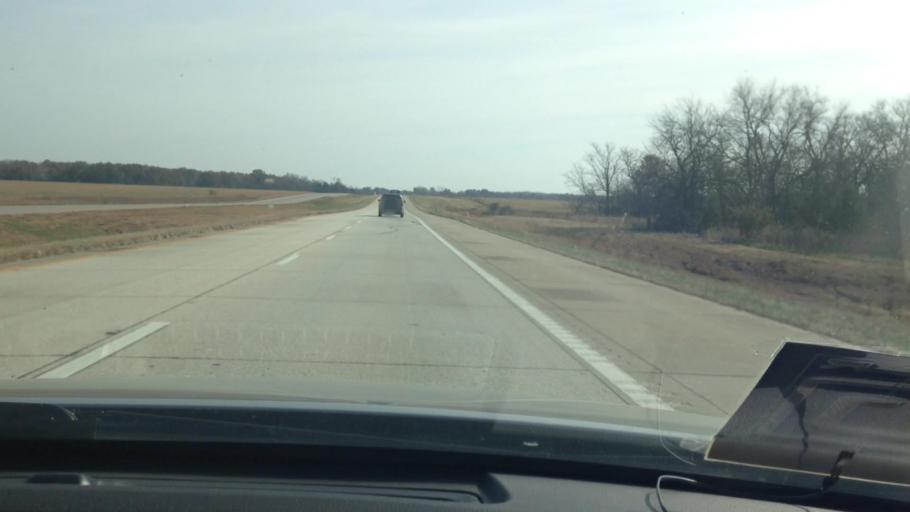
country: US
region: Missouri
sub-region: Henry County
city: Clinton
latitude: 38.4120
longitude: -93.8554
